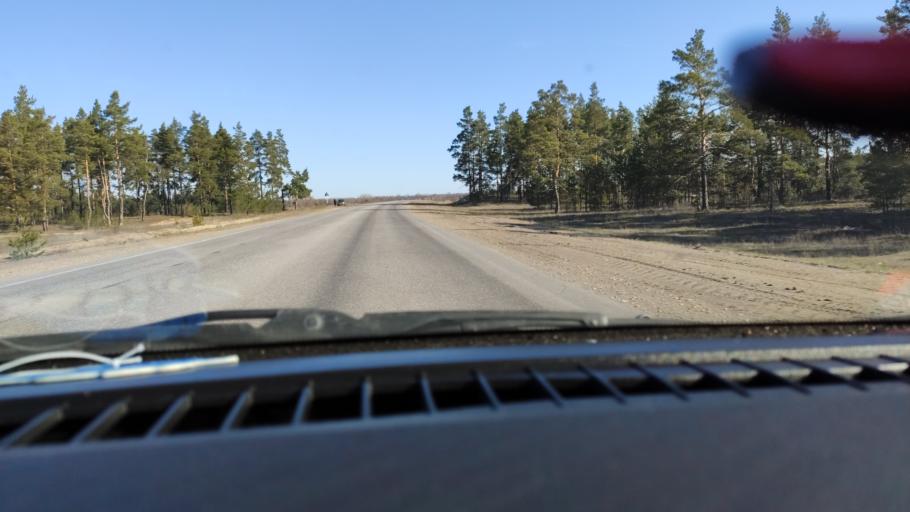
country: RU
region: Samara
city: Varlamovo
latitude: 53.1485
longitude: 48.2842
